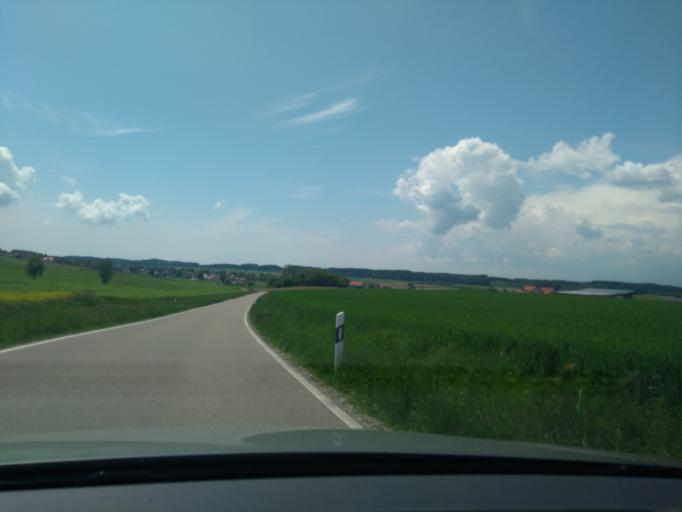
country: DE
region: Baden-Wuerttemberg
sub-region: Tuebingen Region
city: Eberhardzell
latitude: 47.9437
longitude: 9.8306
